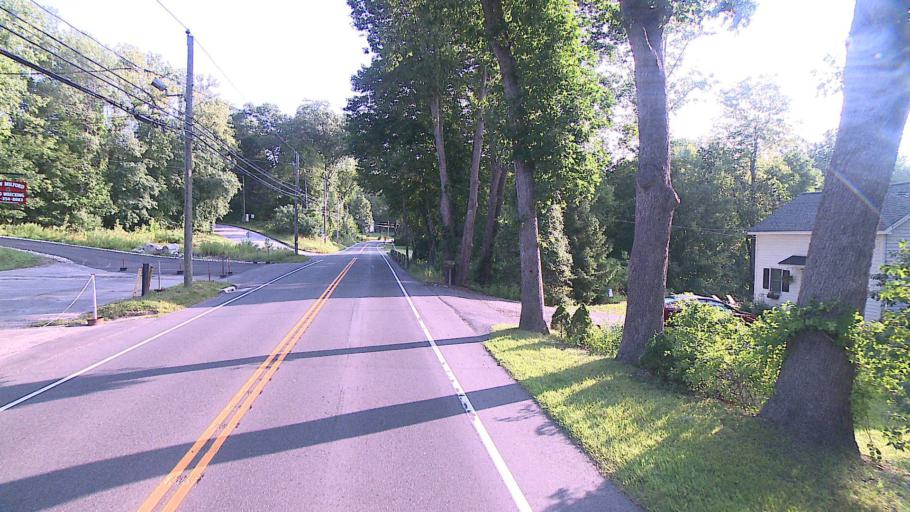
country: US
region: Connecticut
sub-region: Fairfield County
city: Sherman
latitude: 41.6061
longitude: -73.4578
